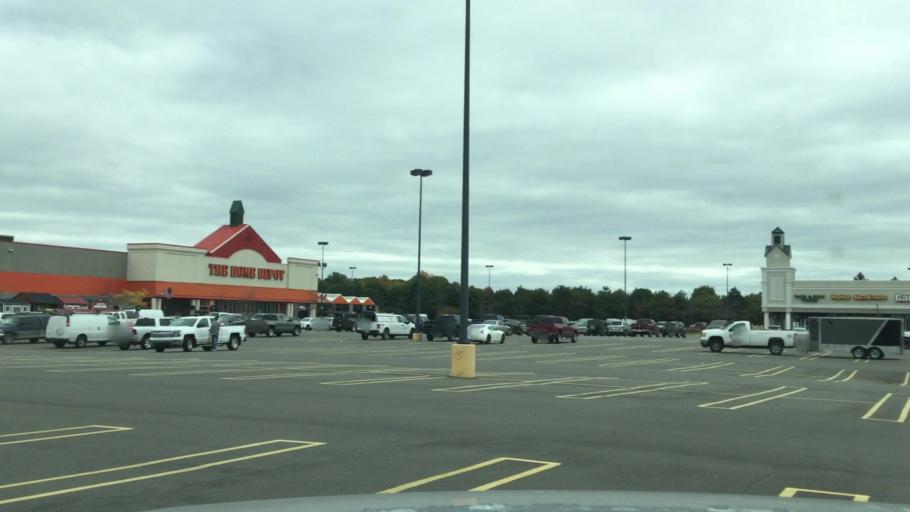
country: US
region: Michigan
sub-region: Oakland County
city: Waterford
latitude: 42.6593
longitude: -83.4668
